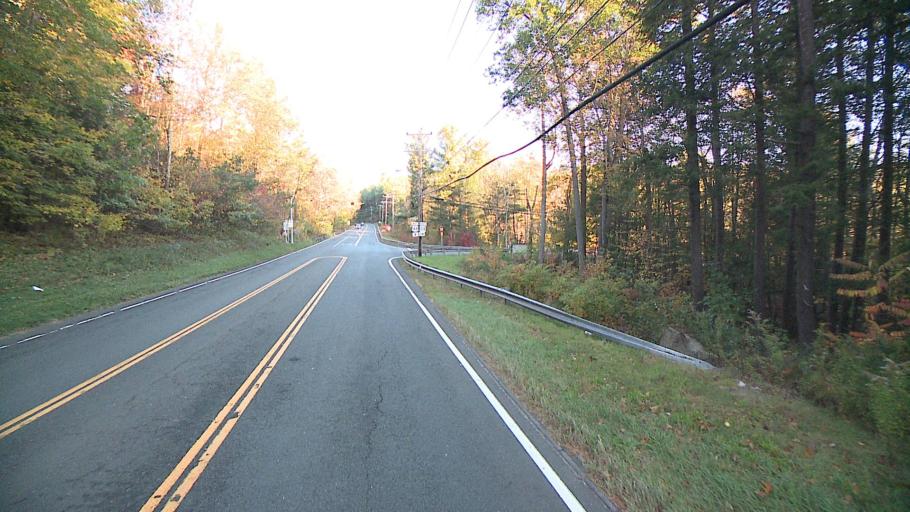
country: US
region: Connecticut
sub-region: Litchfield County
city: New Hartford Center
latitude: 41.9079
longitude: -73.0005
